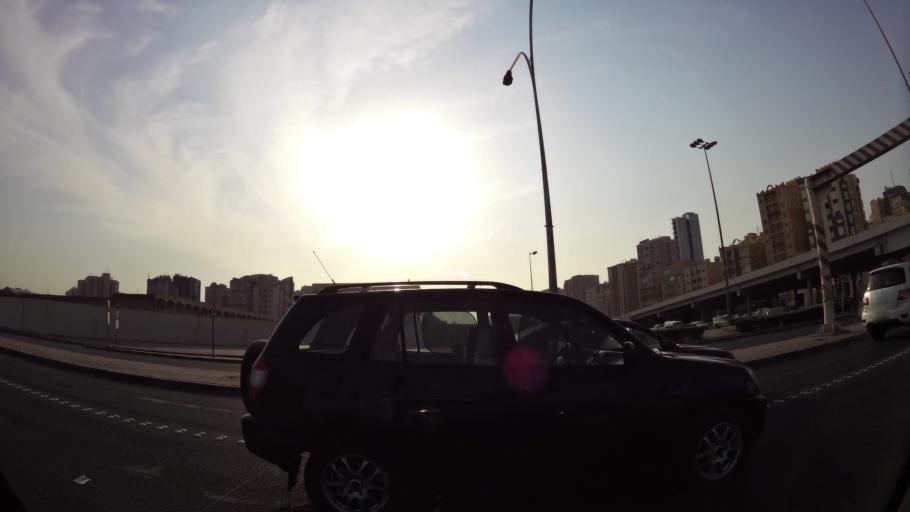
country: KW
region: Muhafazat Hawalli
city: Hawalli
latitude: 29.3277
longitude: 48.0294
